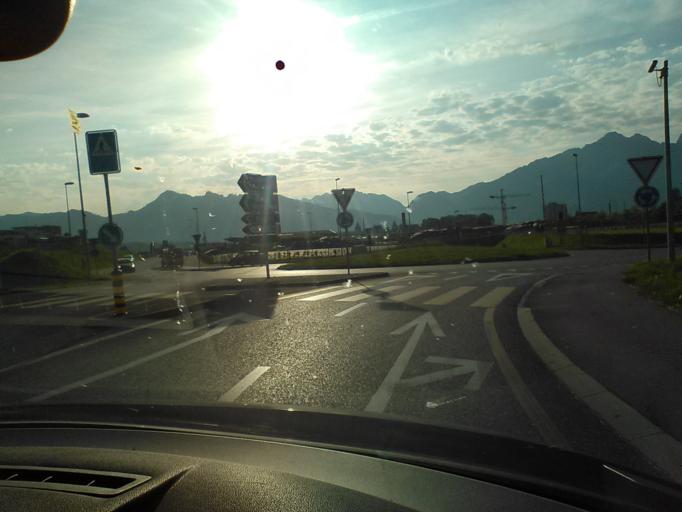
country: CH
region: Fribourg
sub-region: Gruyere District
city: Bulle
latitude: 46.6174
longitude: 7.0428
